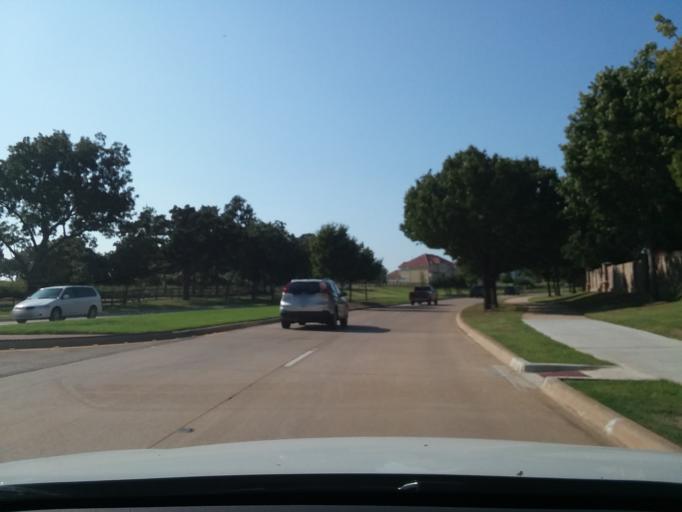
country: US
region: Texas
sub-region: Denton County
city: Flower Mound
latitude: 33.0310
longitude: -97.1045
